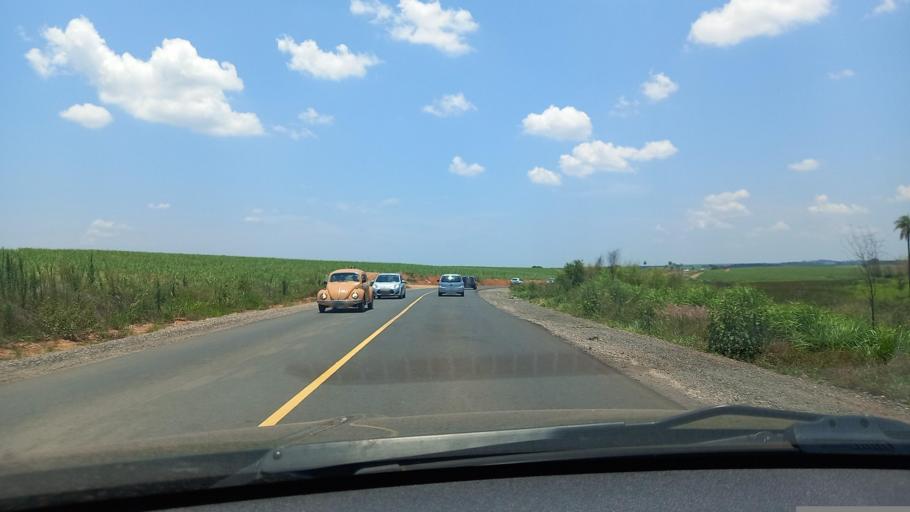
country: BR
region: Sao Paulo
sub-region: Moji-Guacu
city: Mogi-Gaucu
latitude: -22.3598
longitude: -46.8688
